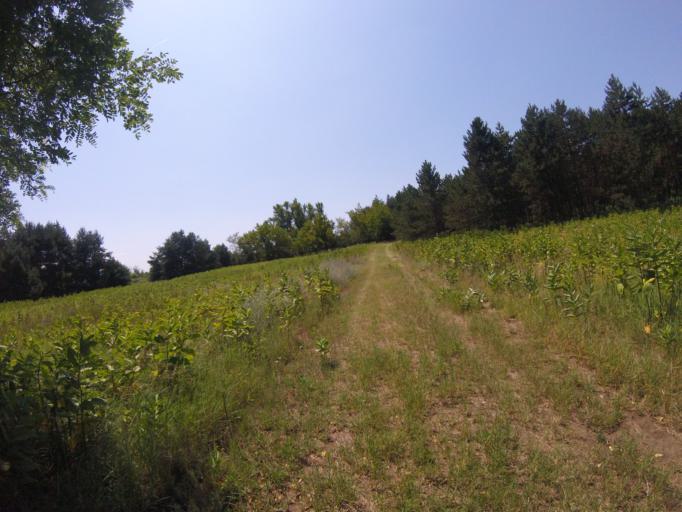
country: HU
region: Bacs-Kiskun
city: Jaszszentlaszlo
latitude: 46.6222
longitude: 19.7141
